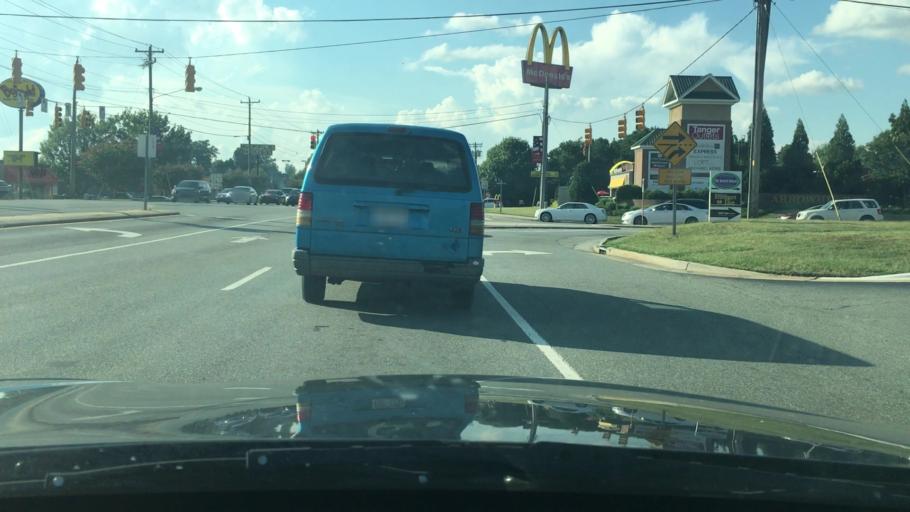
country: US
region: North Carolina
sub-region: Alamance County
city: Mebane
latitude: 36.0728
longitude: -79.2726
